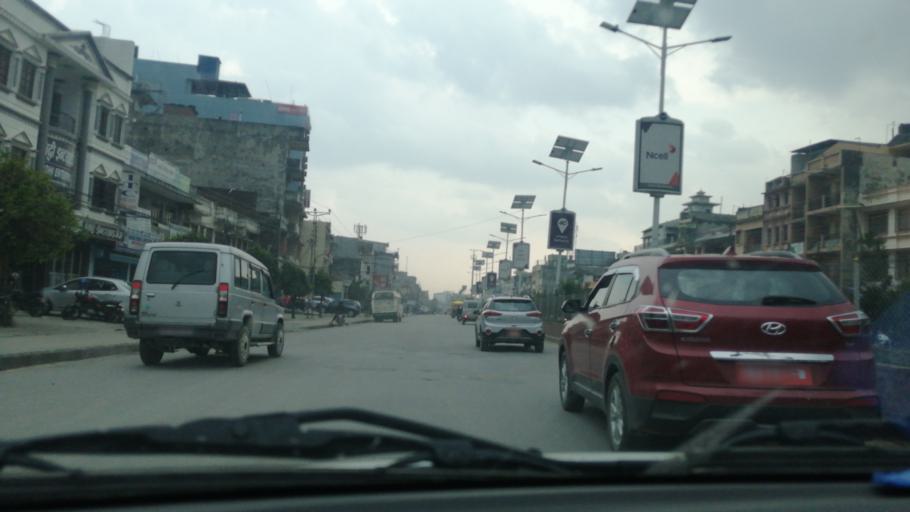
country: NP
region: Western Region
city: Butwal
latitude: 27.7035
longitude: 83.4667
